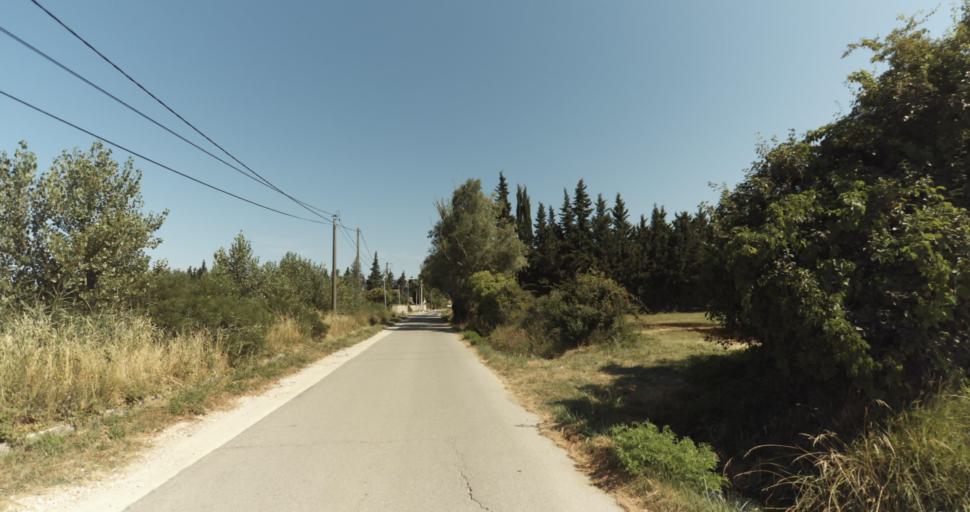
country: FR
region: Provence-Alpes-Cote d'Azur
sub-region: Departement du Vaucluse
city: Monteux
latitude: 44.0207
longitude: 4.9974
